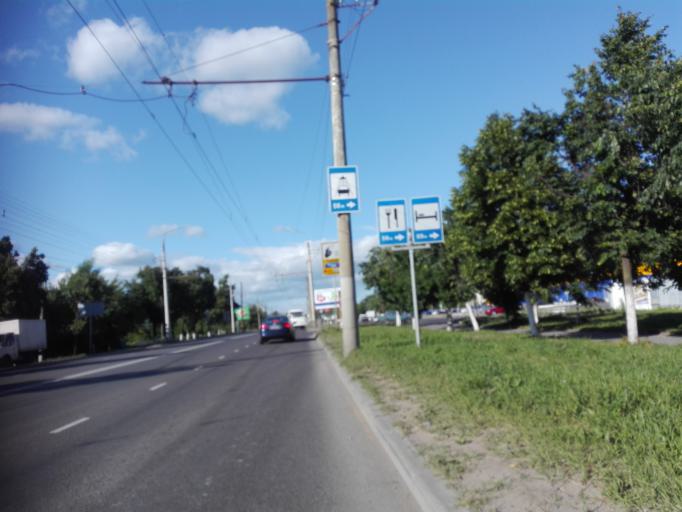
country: RU
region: Orjol
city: Orel
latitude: 52.9896
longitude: 36.1226
